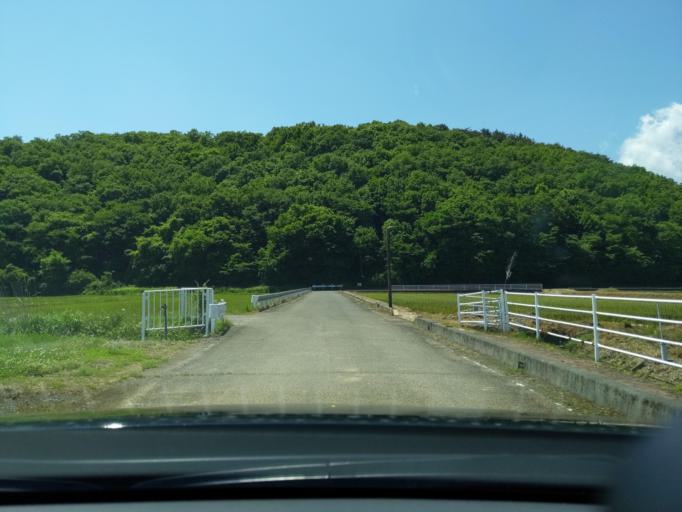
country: JP
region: Fukushima
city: Koriyama
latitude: 37.3904
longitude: 140.2790
